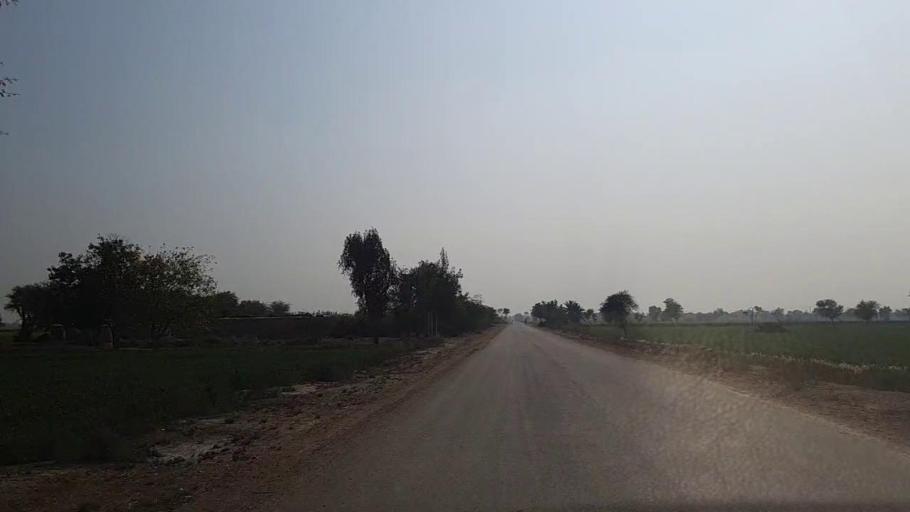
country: PK
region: Sindh
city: Jam Sahib
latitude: 26.3511
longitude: 68.5345
